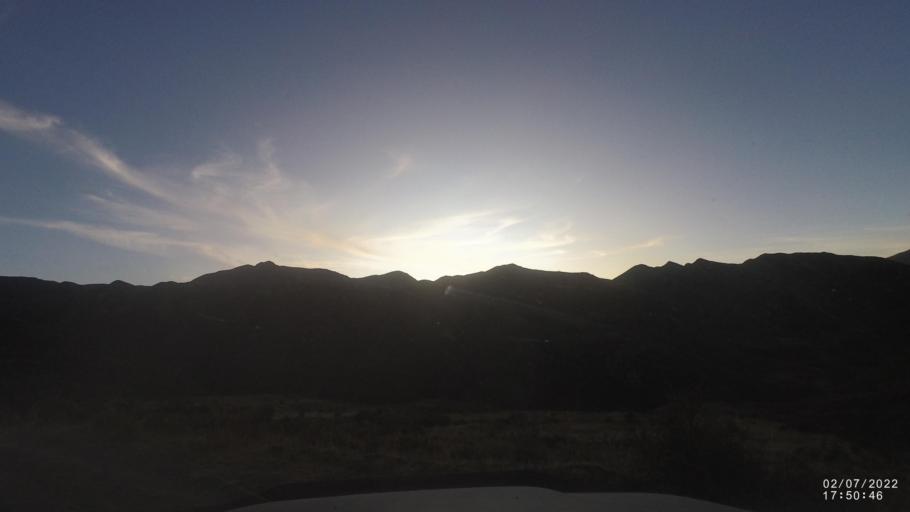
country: BO
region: Cochabamba
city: Irpa Irpa
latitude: -17.8485
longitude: -66.6178
